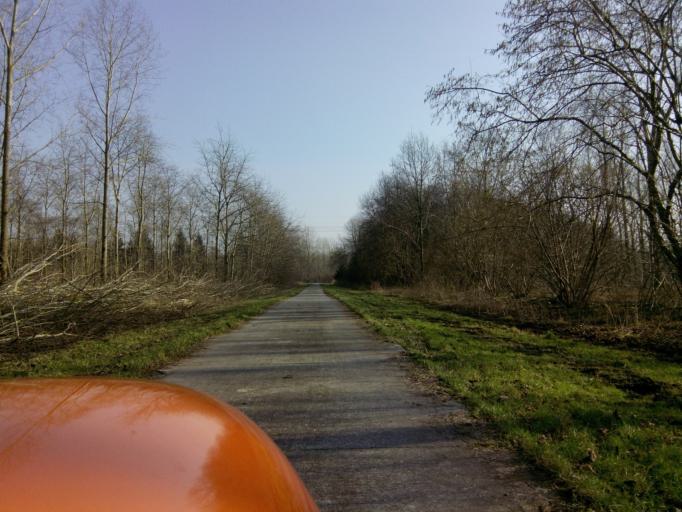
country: NL
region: Flevoland
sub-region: Gemeente Zeewolde
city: Zeewolde
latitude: 52.3386
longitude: 5.4542
